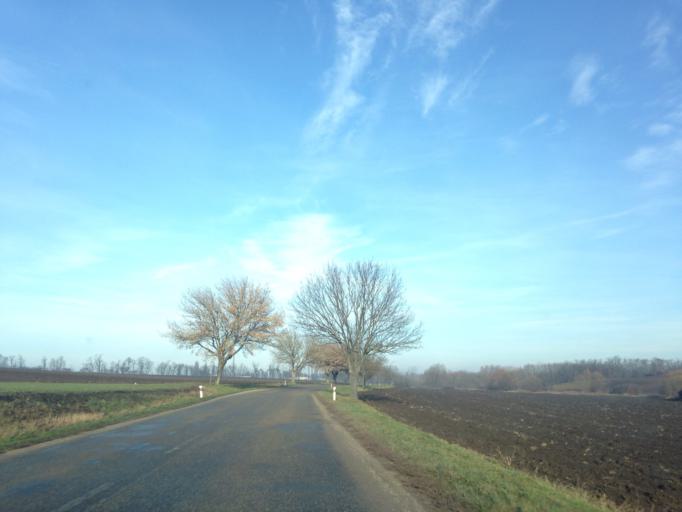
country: SK
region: Nitriansky
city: Svodin
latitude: 47.9718
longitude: 18.4073
